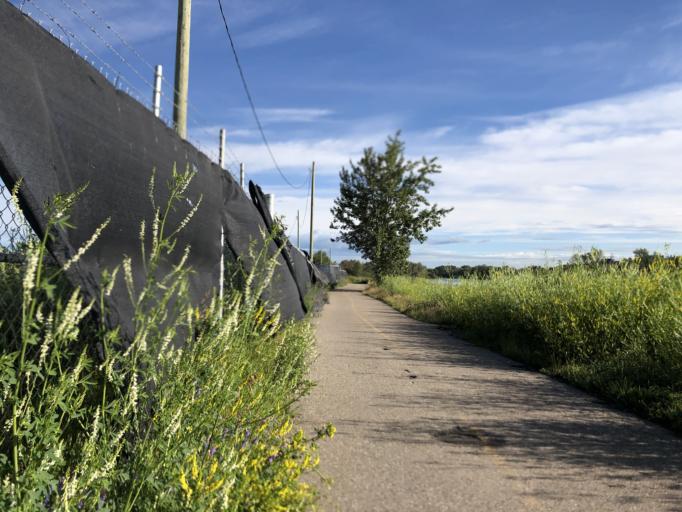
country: CA
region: Alberta
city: Calgary
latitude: 50.9576
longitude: -114.0243
